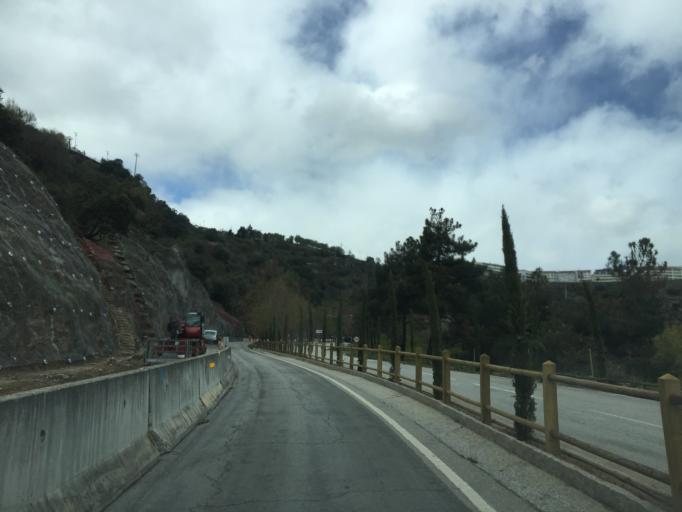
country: PT
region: Braganca
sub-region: Miranda do Douro
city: Miranda do Douro
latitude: 41.4916
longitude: -6.2676
